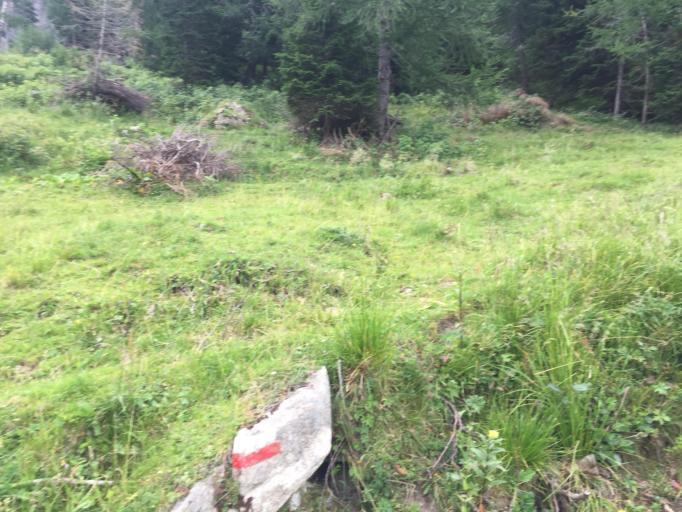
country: IT
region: Friuli Venezia Giulia
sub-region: Provincia di Udine
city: Forni Avoltri
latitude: 46.5975
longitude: 12.8093
